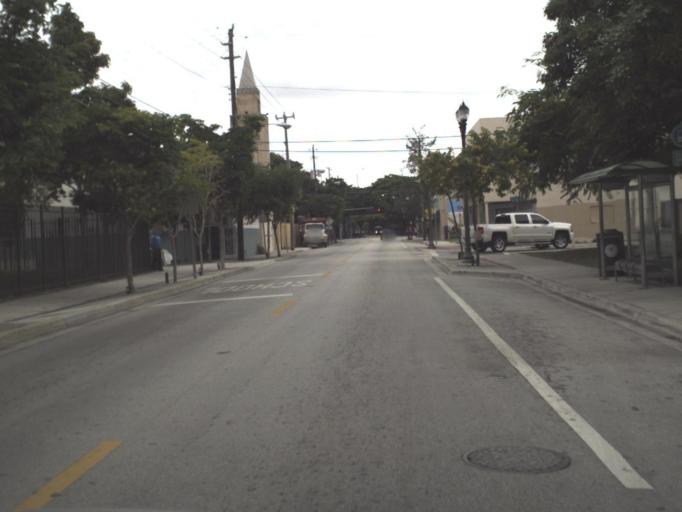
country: US
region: Florida
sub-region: Miami-Dade County
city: Miami
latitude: 25.7864
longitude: -80.1998
